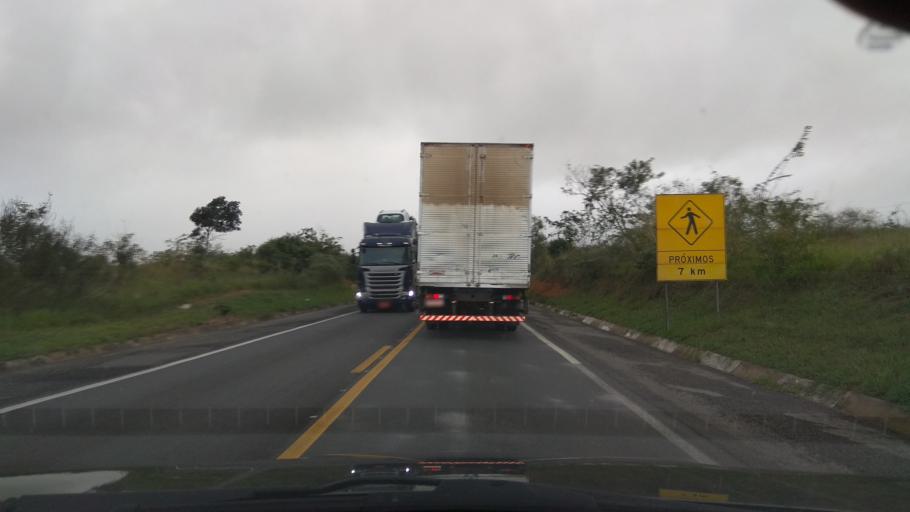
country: BR
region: Bahia
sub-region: Jaguaquara
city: Jaguaquara
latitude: -13.4770
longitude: -40.0406
